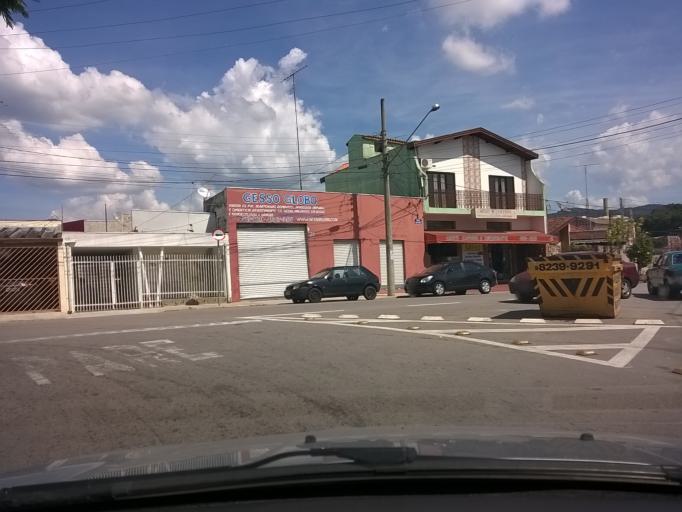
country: BR
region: Sao Paulo
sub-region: Jundiai
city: Jundiai
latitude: -23.2127
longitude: -46.8746
